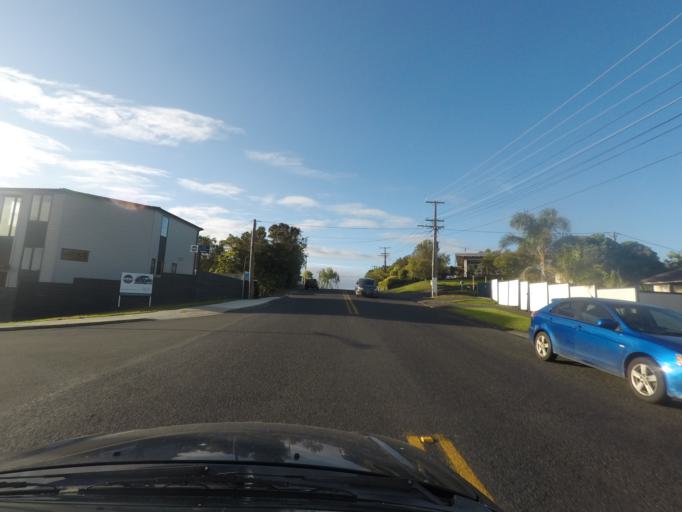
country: NZ
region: Auckland
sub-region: Auckland
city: Waitakere
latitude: -36.9182
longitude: 174.6579
